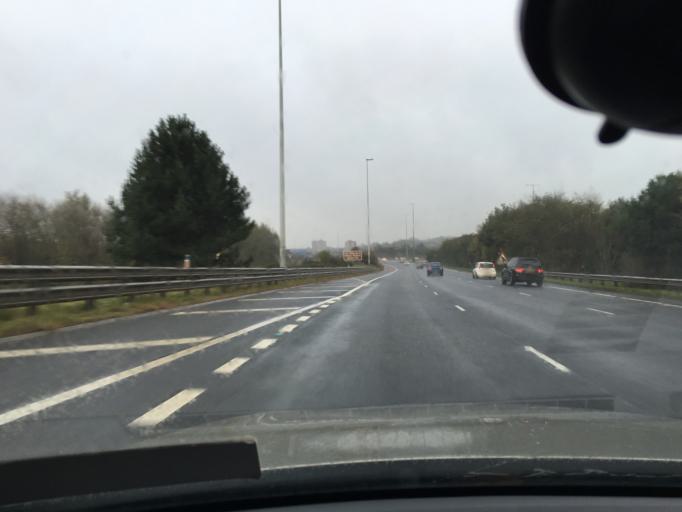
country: GB
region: Northern Ireland
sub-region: Newtownabbey District
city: Newtownabbey
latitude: 54.6428
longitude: -5.9157
